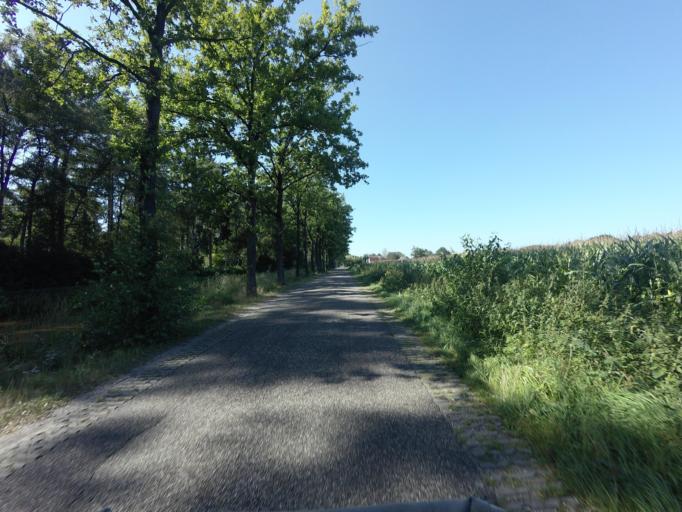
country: NL
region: Overijssel
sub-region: Gemeente Hardenberg
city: Hardenberg
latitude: 52.5328
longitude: 6.6378
